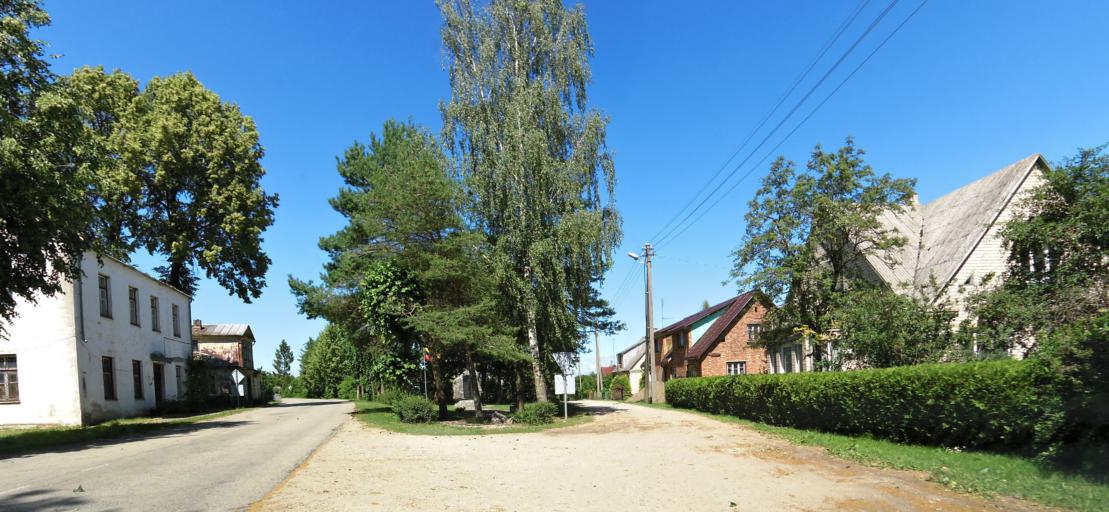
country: LT
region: Panevezys
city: Pasvalys
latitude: 56.2298
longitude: 24.4055
